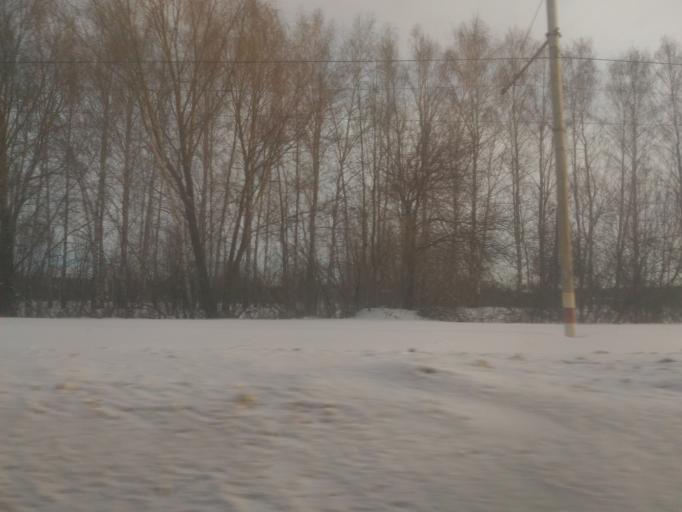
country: RU
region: Ulyanovsk
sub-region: Ulyanovskiy Rayon
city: Ulyanovsk
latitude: 54.3652
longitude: 48.3268
